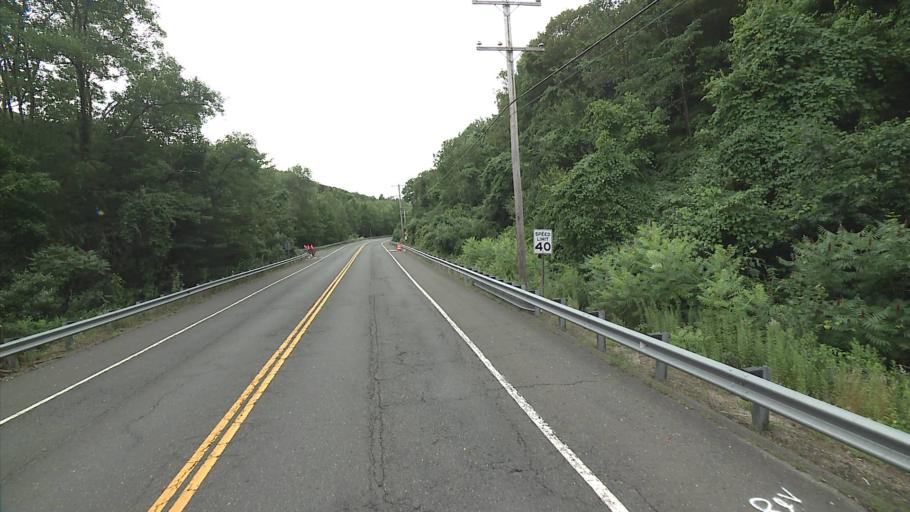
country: US
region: Connecticut
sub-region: Litchfield County
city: Winsted
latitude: 41.9958
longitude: -73.0465
